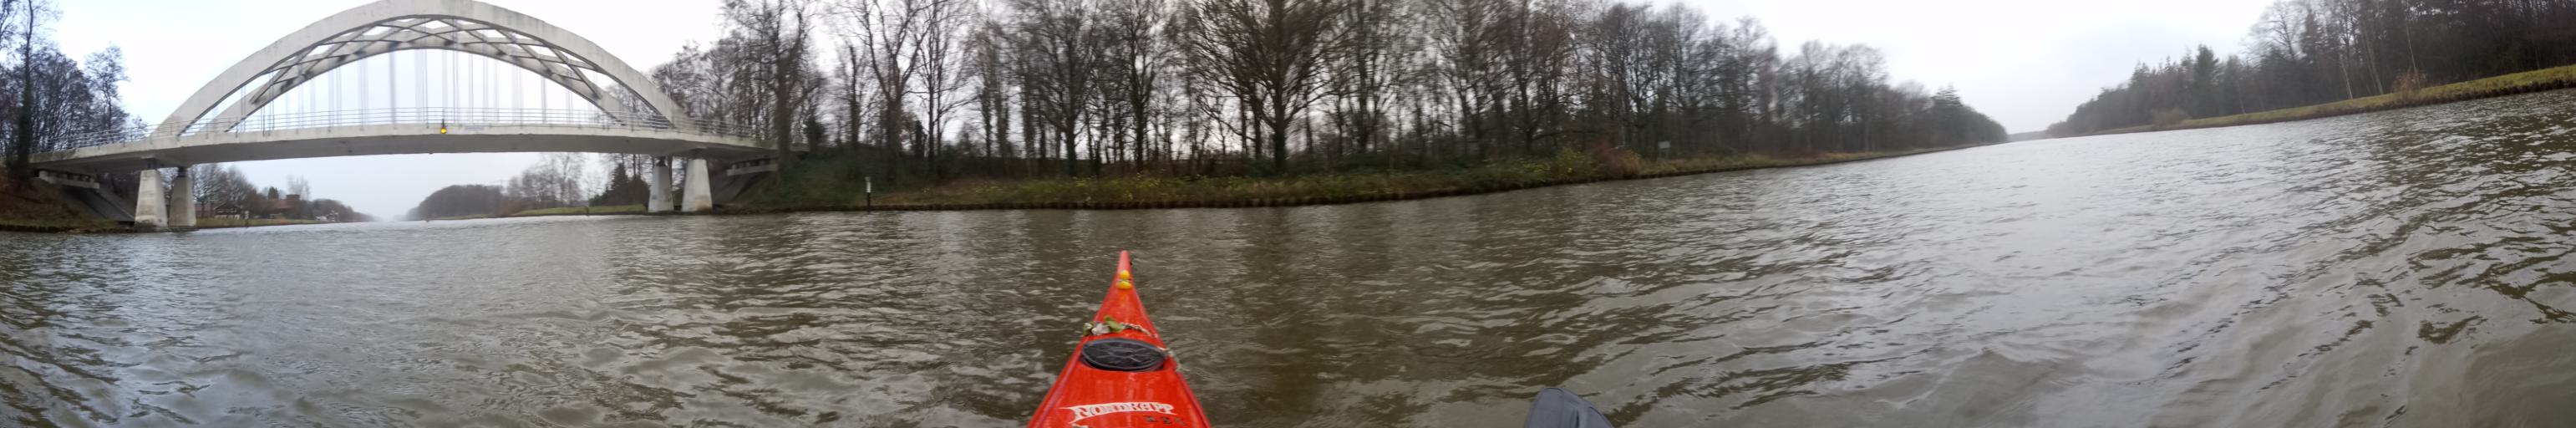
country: NL
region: Gelderland
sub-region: Gemeente Lochem
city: Almen
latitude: 52.1659
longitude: 6.2928
